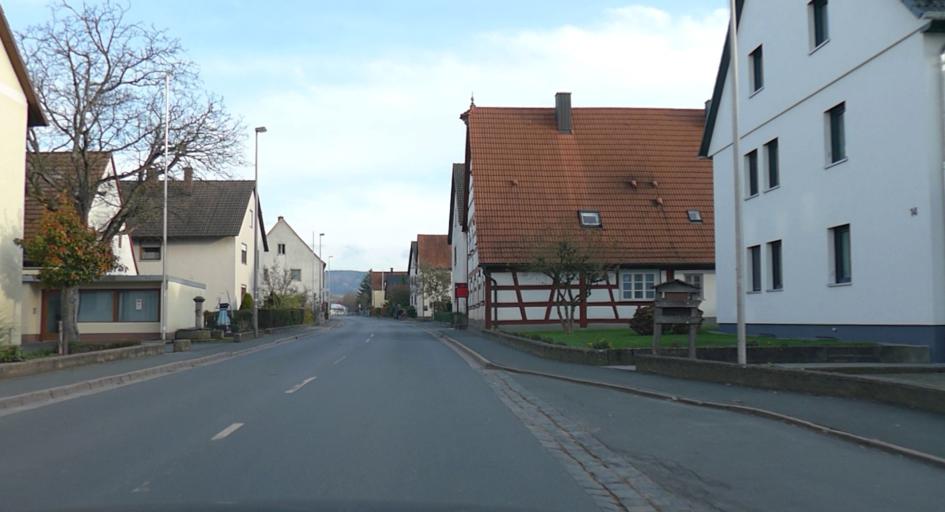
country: DE
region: Bavaria
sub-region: Upper Franconia
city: Poxdorf
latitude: 49.6653
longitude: 11.0715
